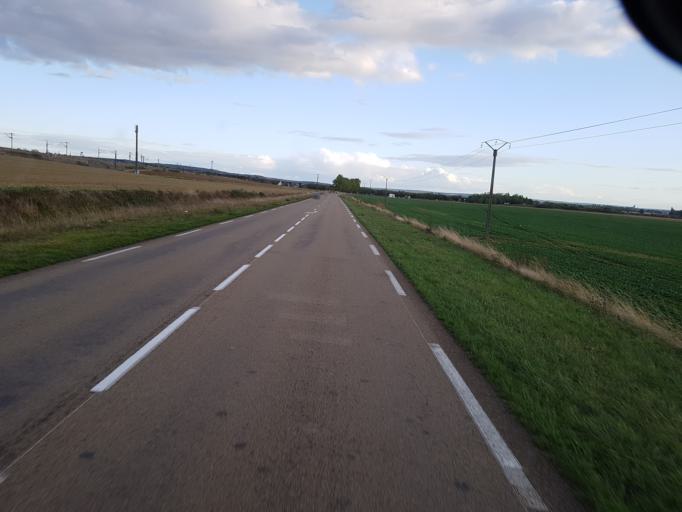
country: FR
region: Bourgogne
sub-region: Departement de l'Yonne
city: Soucy
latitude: 48.2660
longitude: 3.2793
